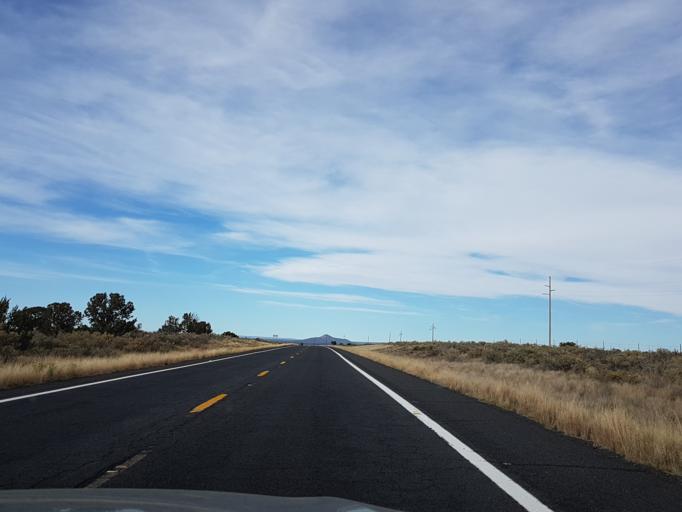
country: US
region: Arizona
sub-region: Coconino County
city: Williams
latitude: 35.6001
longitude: -112.1472
